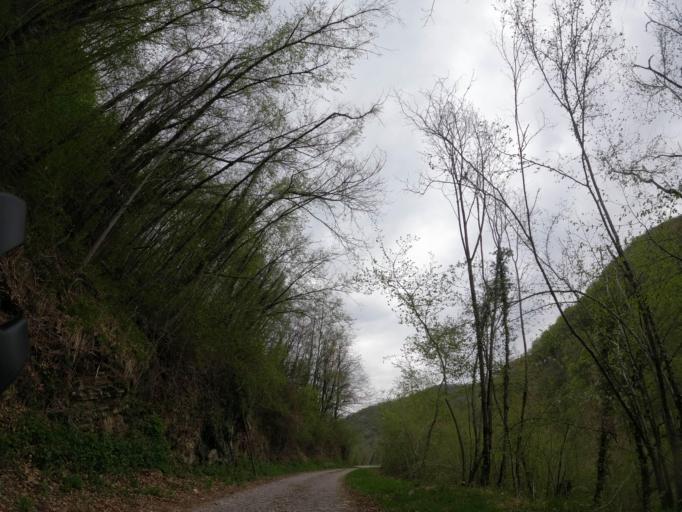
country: SI
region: Kanal
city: Kanal
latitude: 46.1220
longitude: 13.6183
